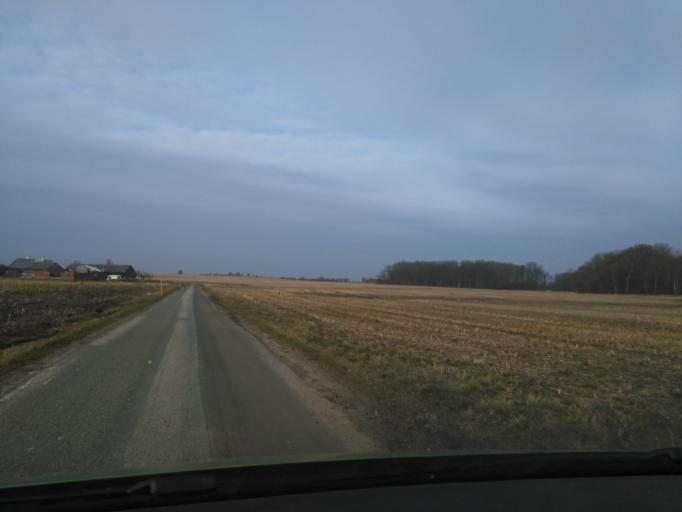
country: DK
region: Central Jutland
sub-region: Odder Kommune
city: Odder
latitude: 55.8743
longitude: 10.1465
